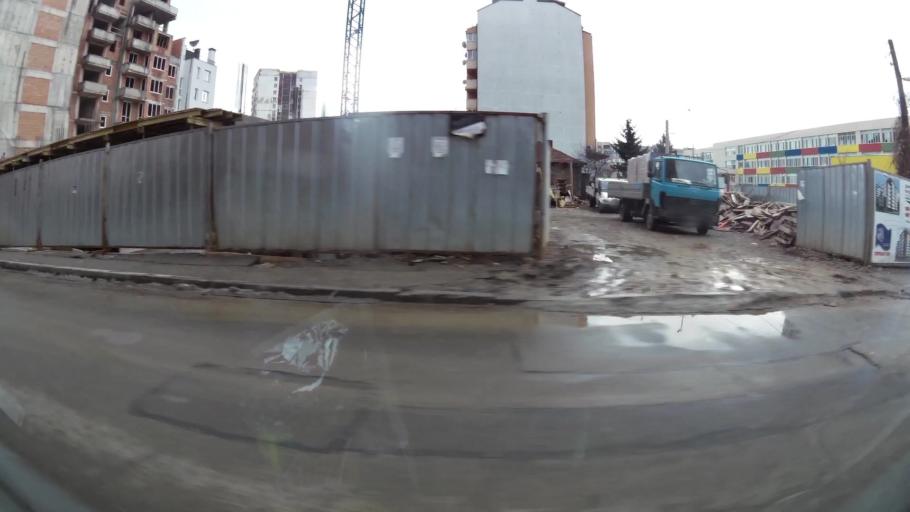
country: BG
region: Sofia-Capital
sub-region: Stolichna Obshtina
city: Sofia
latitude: 42.7288
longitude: 23.2955
